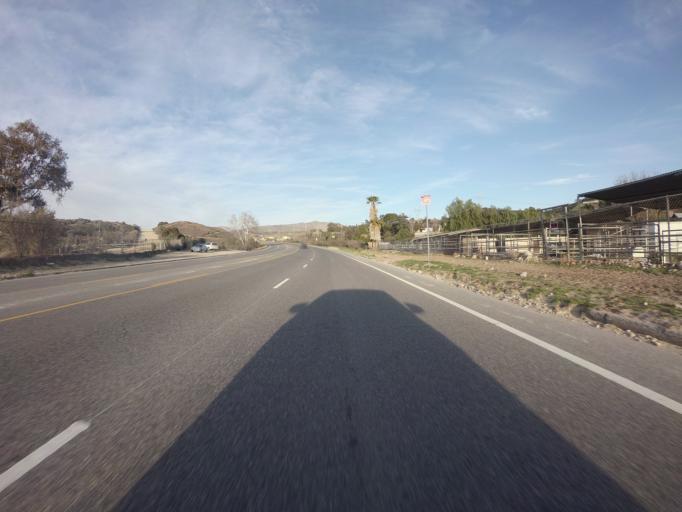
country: US
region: California
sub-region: Los Angeles County
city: San Fernando
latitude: 34.2575
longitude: -118.3740
